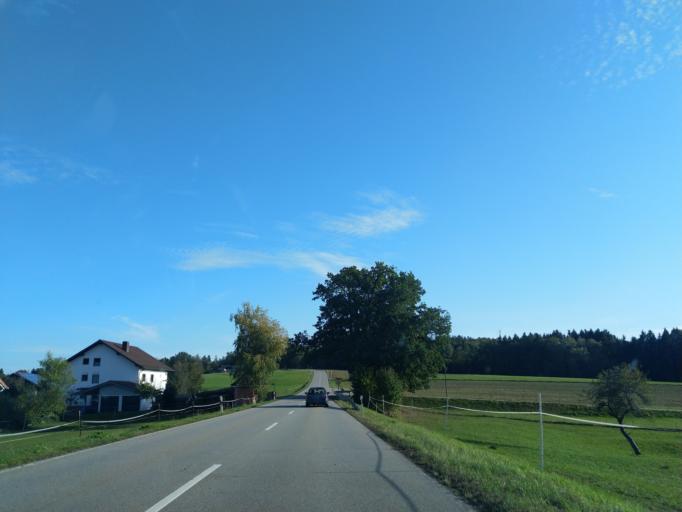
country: DE
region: Bavaria
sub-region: Lower Bavaria
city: Deggendorf
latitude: 48.8574
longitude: 12.9416
